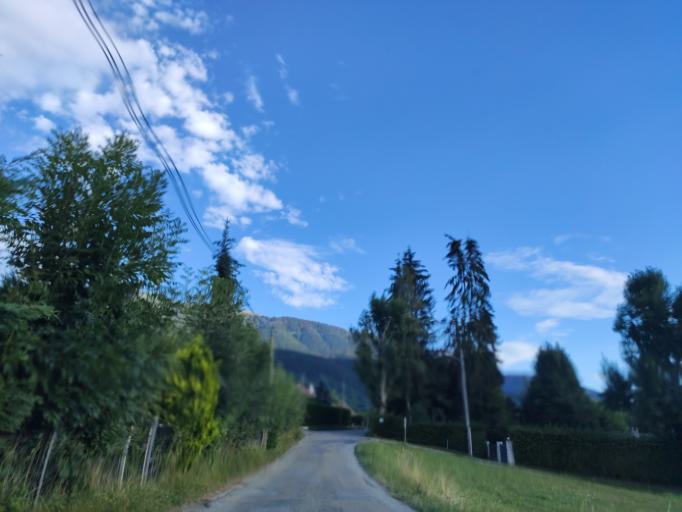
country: FR
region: Rhone-Alpes
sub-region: Departement de l'Isere
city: Revel
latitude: 45.1598
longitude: 5.8521
